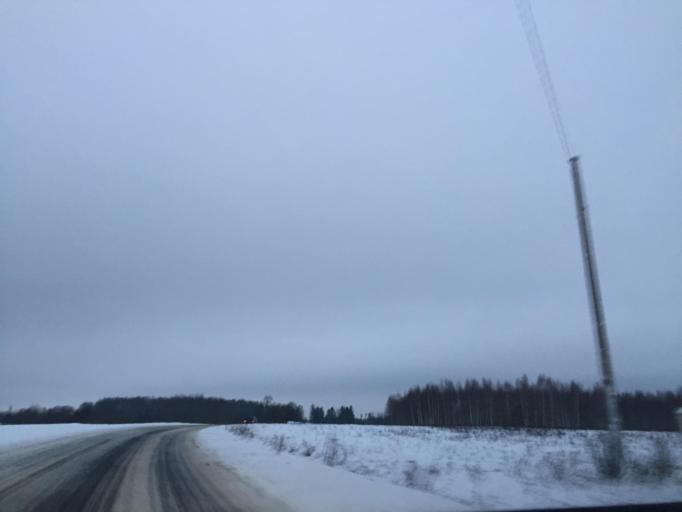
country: LV
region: Smiltene
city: Smiltene
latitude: 57.4358
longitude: 25.7453
